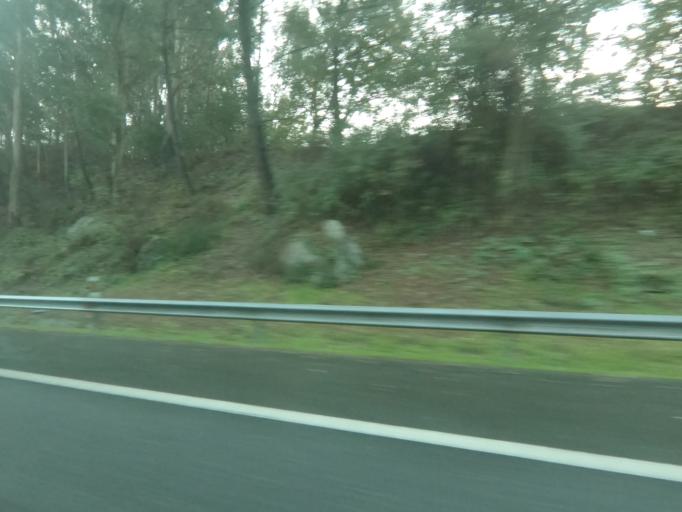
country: ES
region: Galicia
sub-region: Provincia de Pontevedra
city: Tui
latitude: 42.0642
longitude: -8.6483
